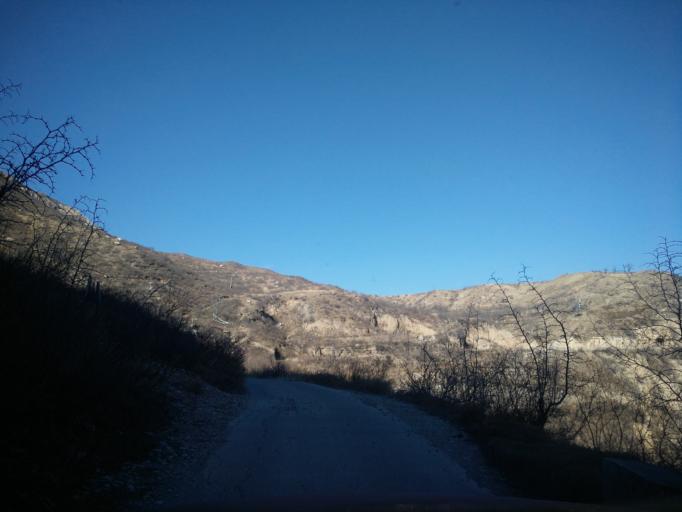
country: CN
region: Beijing
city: Zhaitang
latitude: 40.1537
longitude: 115.6797
